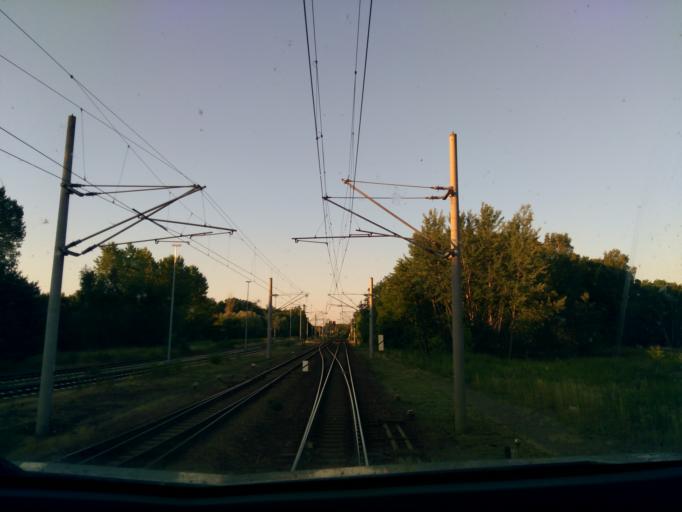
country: DE
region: Brandenburg
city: Konigs Wusterhausen
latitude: 52.2894
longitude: 13.6313
